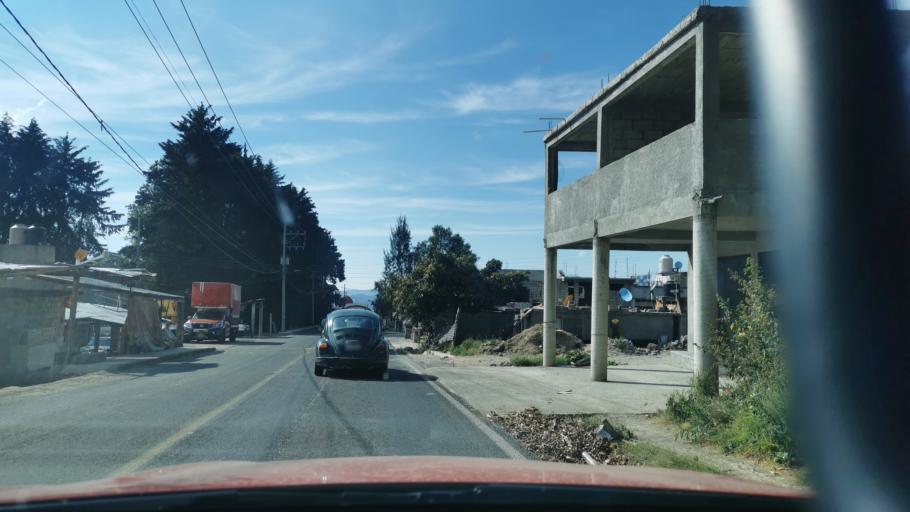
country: MX
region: Mexico
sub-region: Amanalco
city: Polvillos (San Bartolo Quinta Seccion)
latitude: 19.2357
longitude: -100.0775
